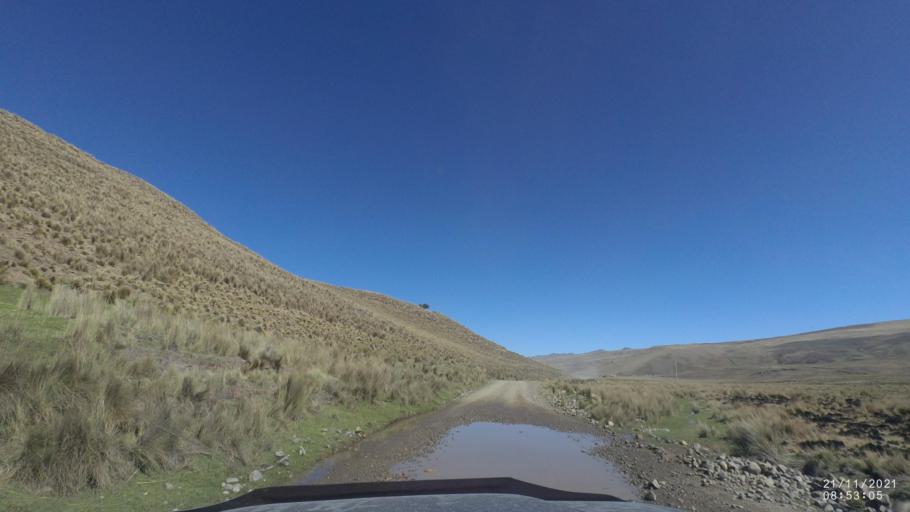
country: BO
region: Cochabamba
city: Cochabamba
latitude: -17.2102
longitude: -66.2407
